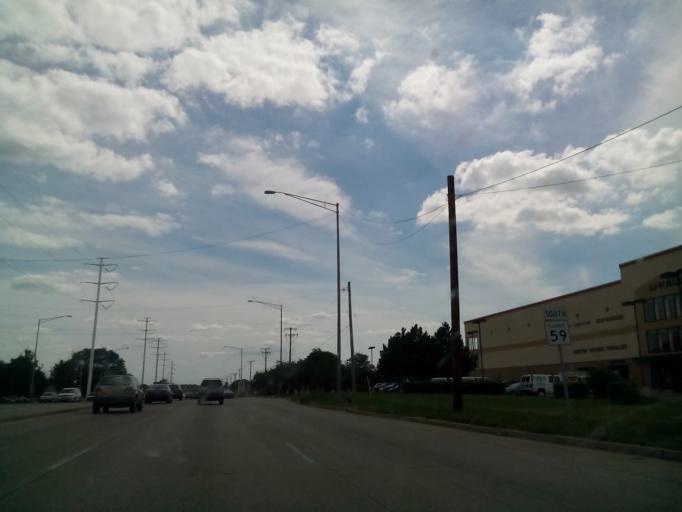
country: US
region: Illinois
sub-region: DuPage County
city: Naperville
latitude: 41.7530
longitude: -88.2061
